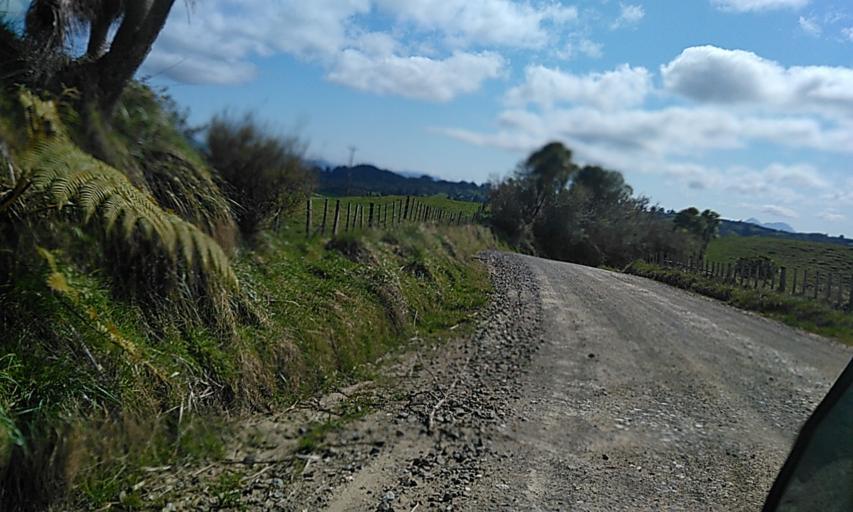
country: NZ
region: Gisborne
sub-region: Gisborne District
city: Gisborne
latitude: -38.2242
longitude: 178.0704
